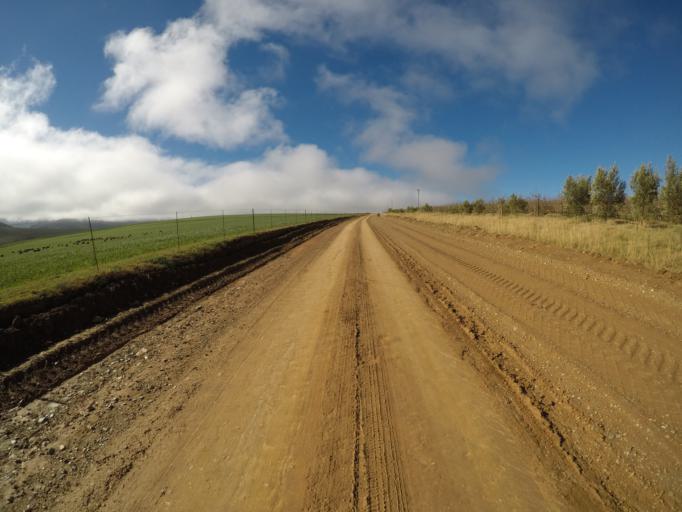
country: ZA
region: Western Cape
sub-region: Overberg District Municipality
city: Caledon
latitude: -34.1092
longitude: 19.7561
